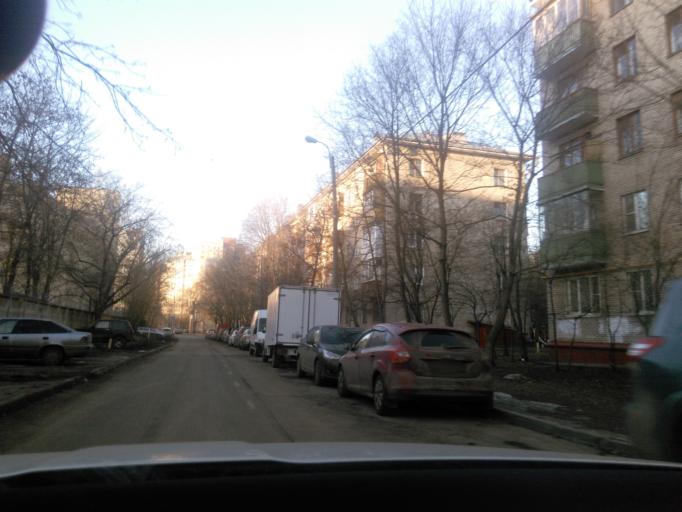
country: RU
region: Moskovskaya
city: Koptevo
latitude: 55.8204
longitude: 37.5286
